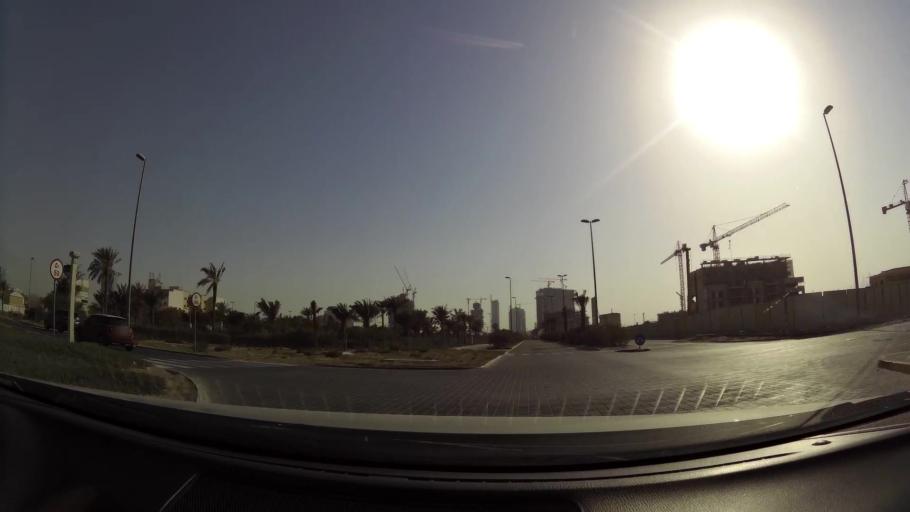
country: AE
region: Dubai
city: Dubai
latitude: 25.0592
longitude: 55.2147
